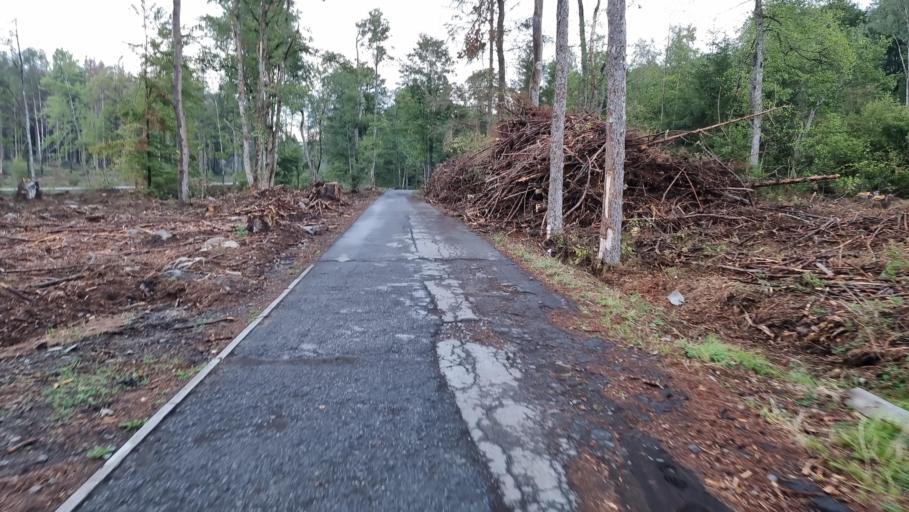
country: DE
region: Lower Saxony
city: Braunlage
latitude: 51.7374
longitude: 10.6128
